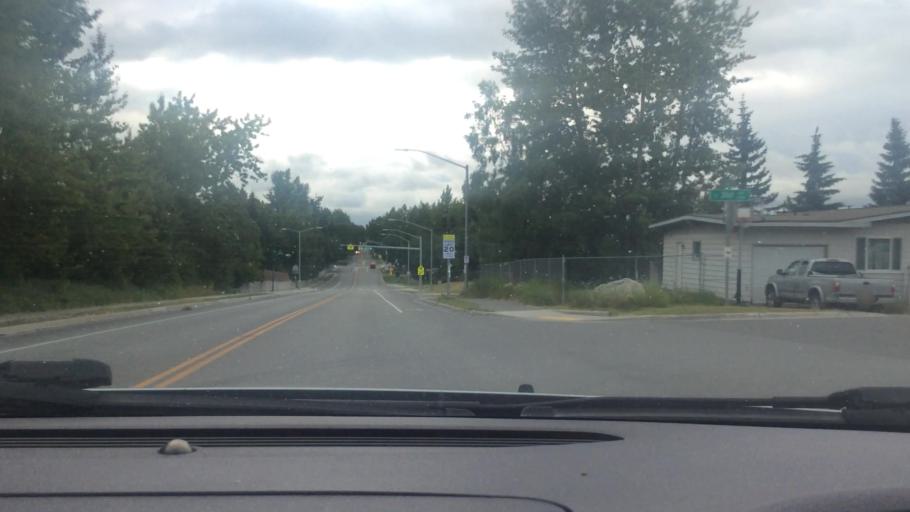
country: US
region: Alaska
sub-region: Anchorage Municipality
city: Anchorage
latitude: 61.1922
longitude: -149.7634
